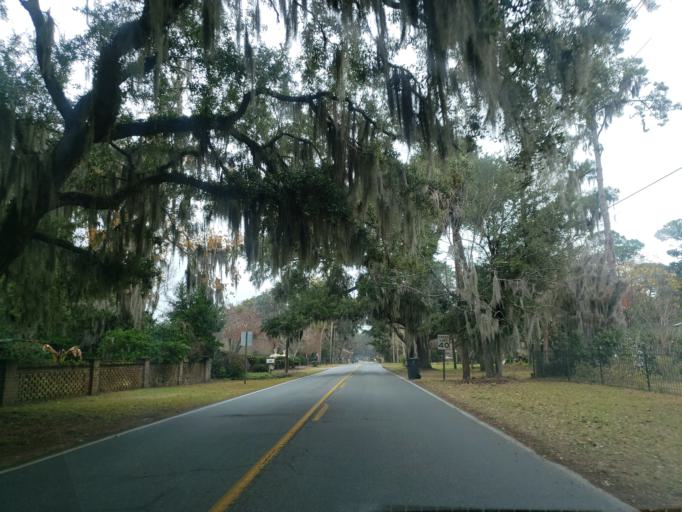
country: US
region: Georgia
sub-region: Chatham County
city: Wilmington Island
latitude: 31.9841
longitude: -80.9955
